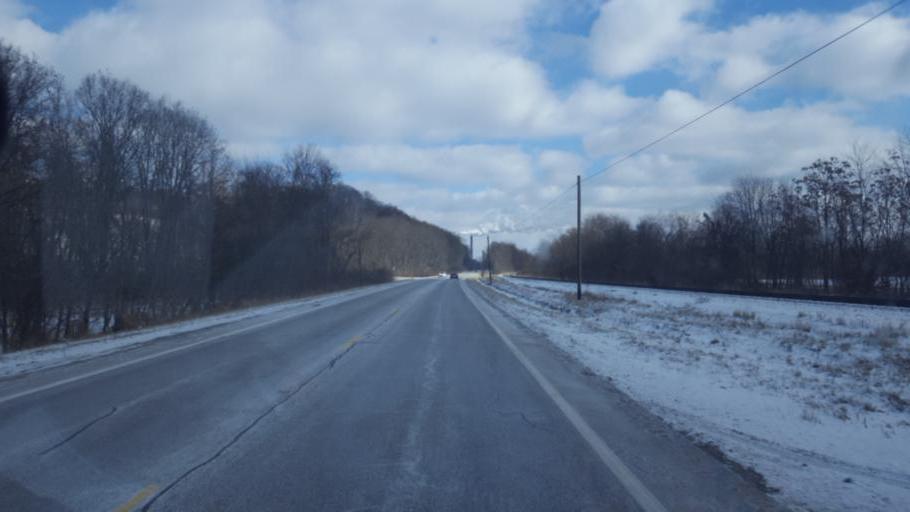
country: US
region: Ohio
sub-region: Muskingum County
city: Dresden
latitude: 40.1652
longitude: -81.9219
